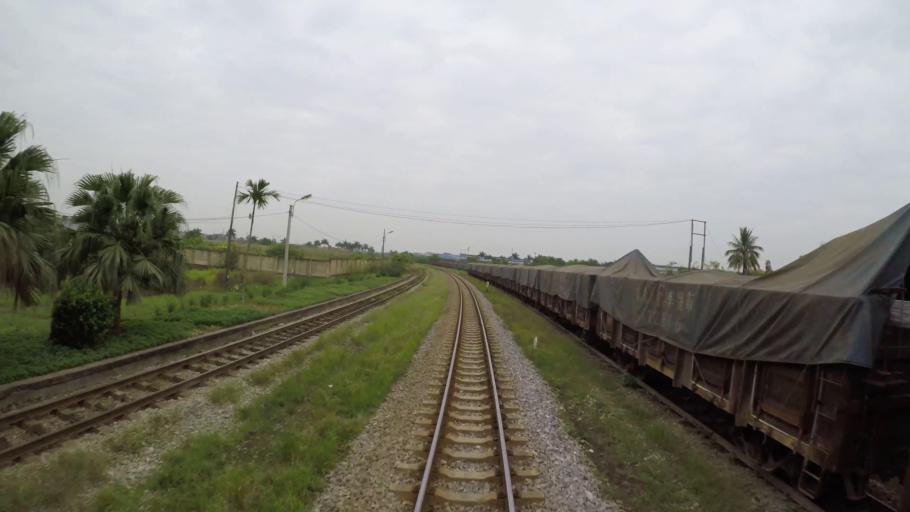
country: VN
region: Hai Phong
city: An Duong
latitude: 20.9060
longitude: 106.5746
